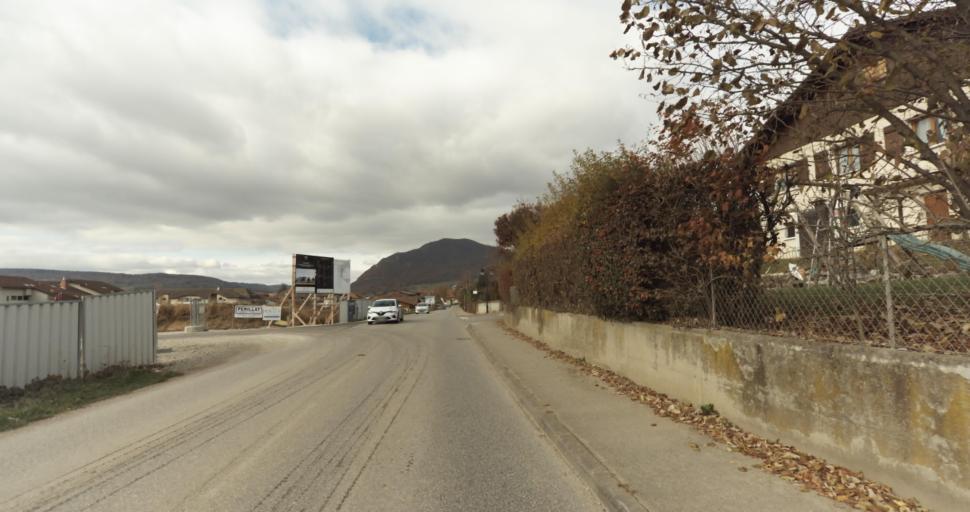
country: FR
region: Rhone-Alpes
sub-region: Departement de la Haute-Savoie
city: Epagny
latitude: 45.9381
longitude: 6.0967
